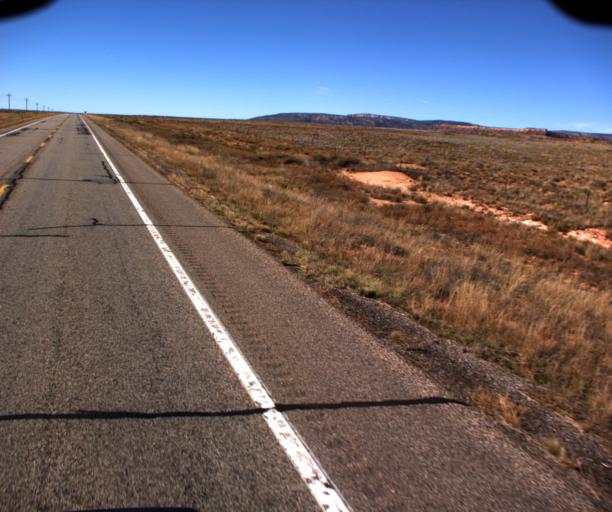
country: US
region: Arizona
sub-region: Coconino County
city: Fredonia
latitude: 36.8899
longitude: -112.6225
